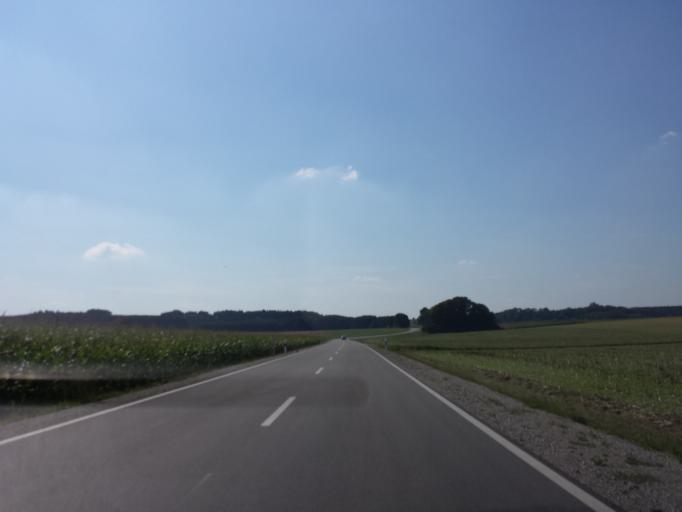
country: DE
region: Bavaria
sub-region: Swabia
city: Tussenhausen
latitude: 48.0725
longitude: 10.5727
